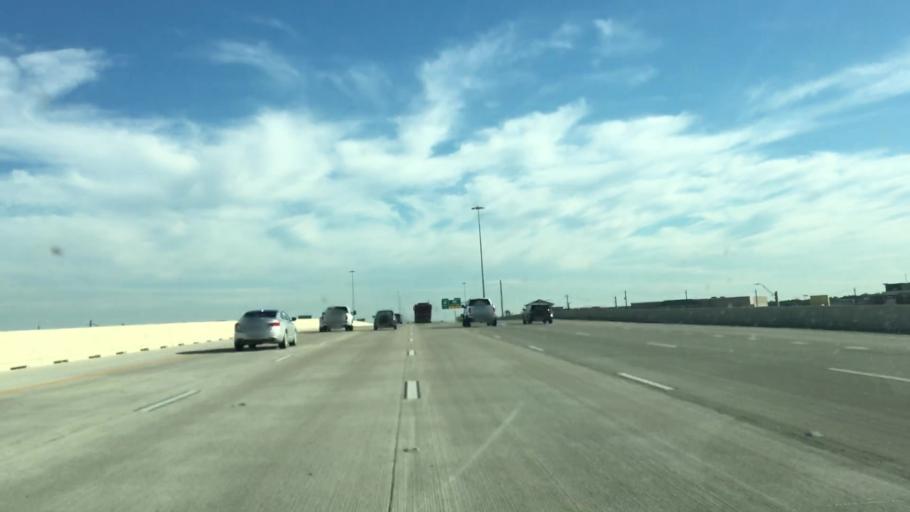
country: US
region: Texas
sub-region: Harris County
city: Webster
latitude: 29.5416
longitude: -95.1428
